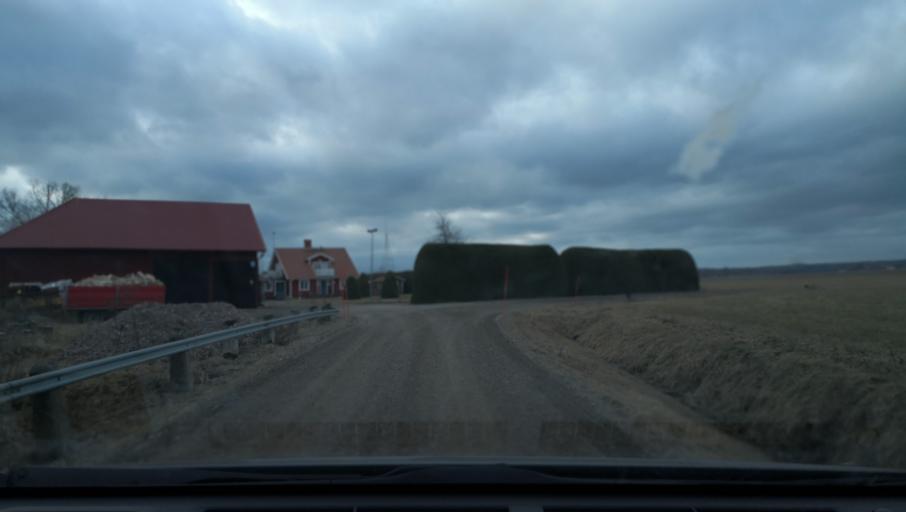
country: SE
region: Vaestmanland
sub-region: Kopings Kommun
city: Koping
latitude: 59.5189
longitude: 15.9158
